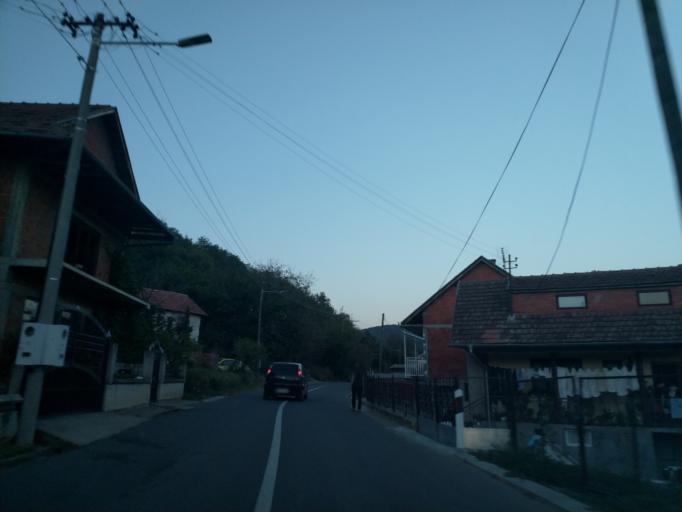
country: RS
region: Central Serbia
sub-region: Rasinski Okrug
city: Krusevac
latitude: 43.6239
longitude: 21.3617
